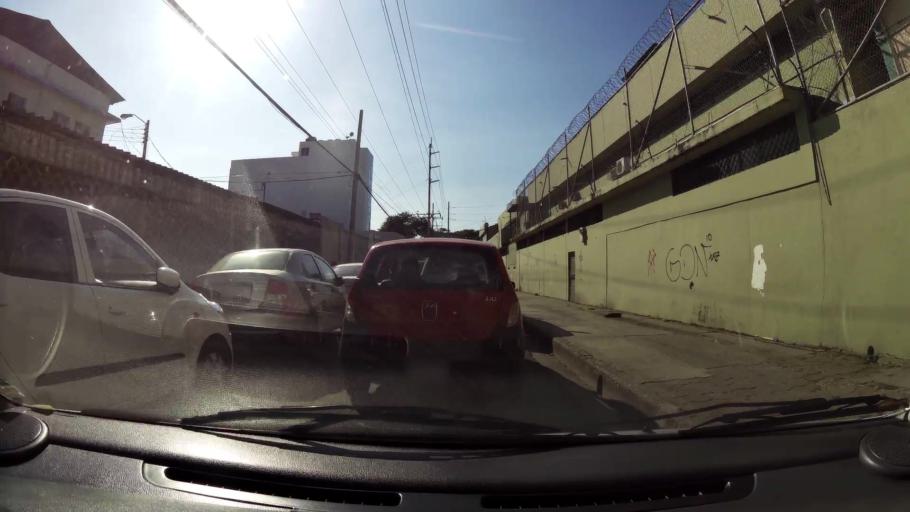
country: EC
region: Guayas
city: Guayaquil
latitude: -2.1774
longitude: -79.8928
